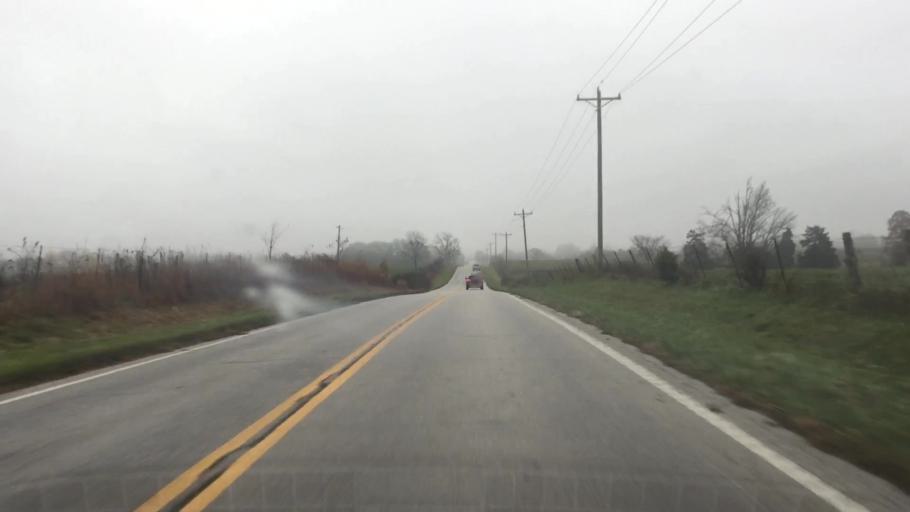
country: US
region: Missouri
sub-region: Callaway County
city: Fulton
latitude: 38.8739
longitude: -92.0562
